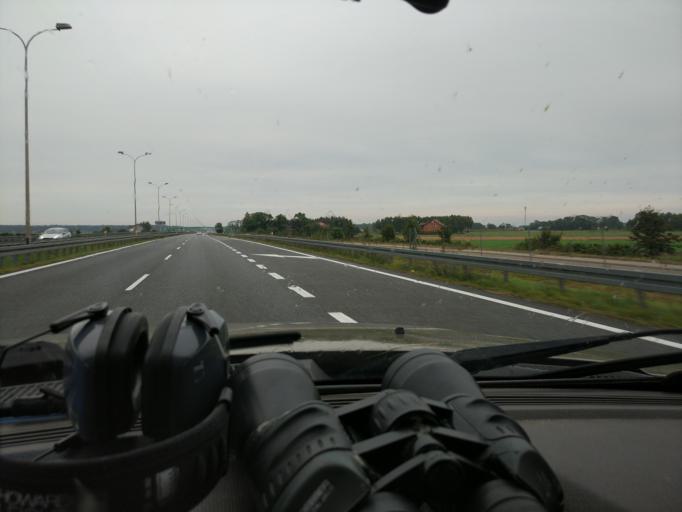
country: PL
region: Masovian Voivodeship
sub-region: Powiat wolominski
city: Dabrowka
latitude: 52.4834
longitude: 21.3484
